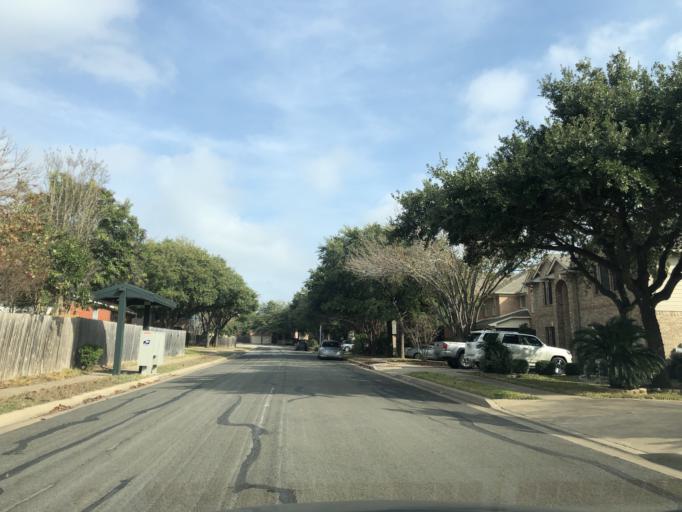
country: US
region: Texas
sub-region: Travis County
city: Wells Branch
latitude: 30.4202
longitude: -97.6804
